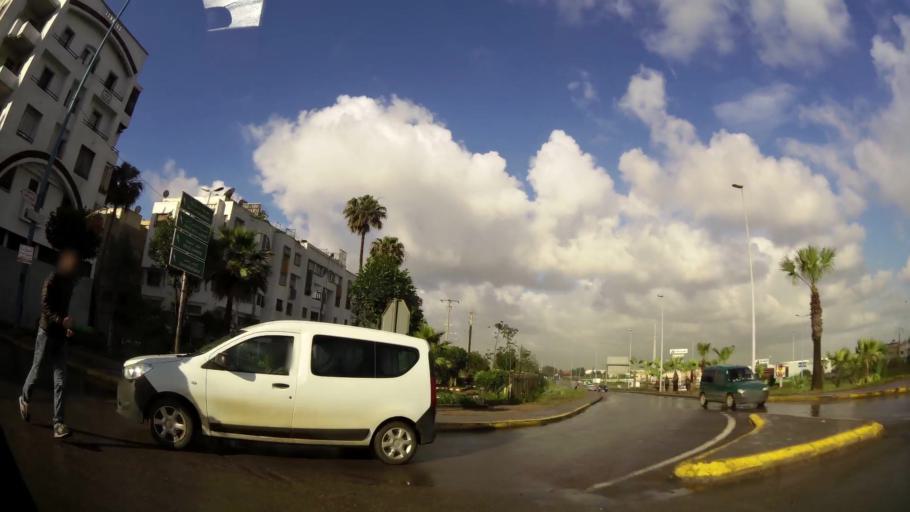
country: MA
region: Grand Casablanca
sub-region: Mediouna
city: Tit Mellil
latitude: 33.5949
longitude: -7.5187
